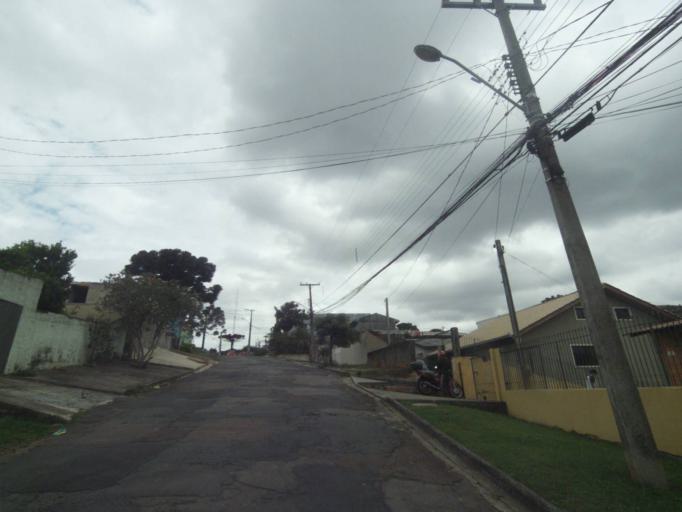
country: BR
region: Parana
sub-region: Curitiba
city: Curitiba
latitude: -25.3900
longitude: -49.2849
